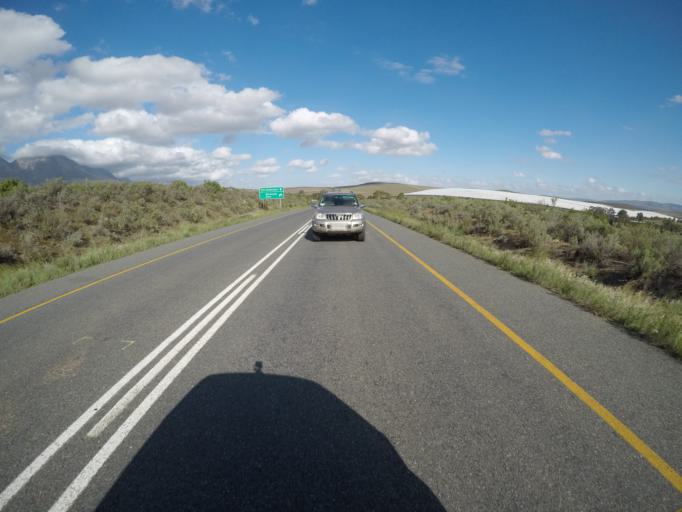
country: ZA
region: Western Cape
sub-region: Overberg District Municipality
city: Swellendam
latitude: -33.9582
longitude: 20.2377
